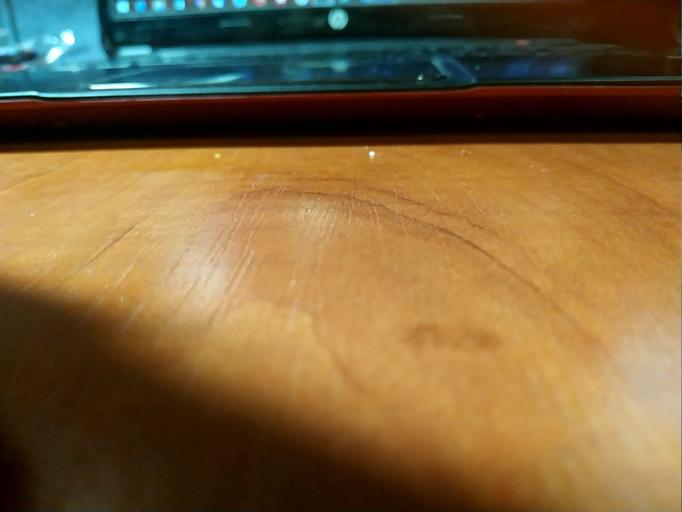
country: RU
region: Tverskaya
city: Vasil'yevskiy Mokh
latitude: 57.1585
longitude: 35.9963
